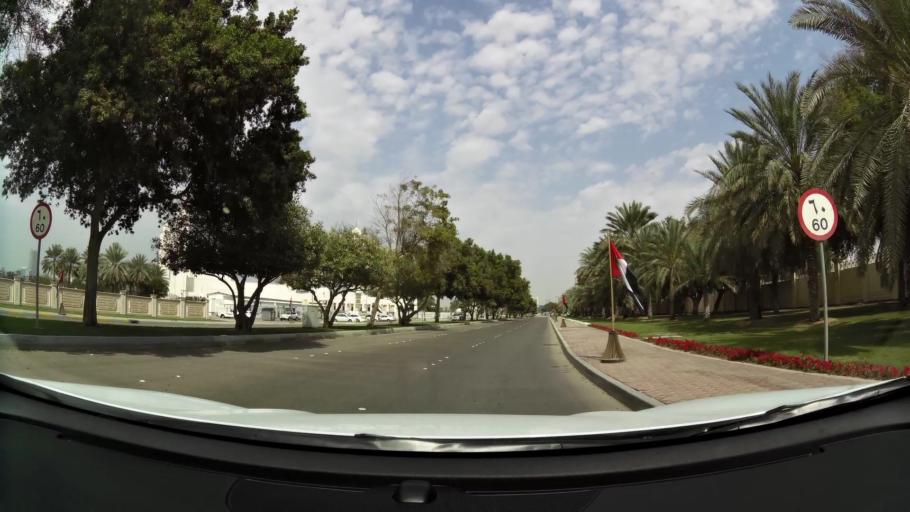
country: AE
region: Abu Dhabi
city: Abu Dhabi
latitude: 24.4501
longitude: 54.3484
